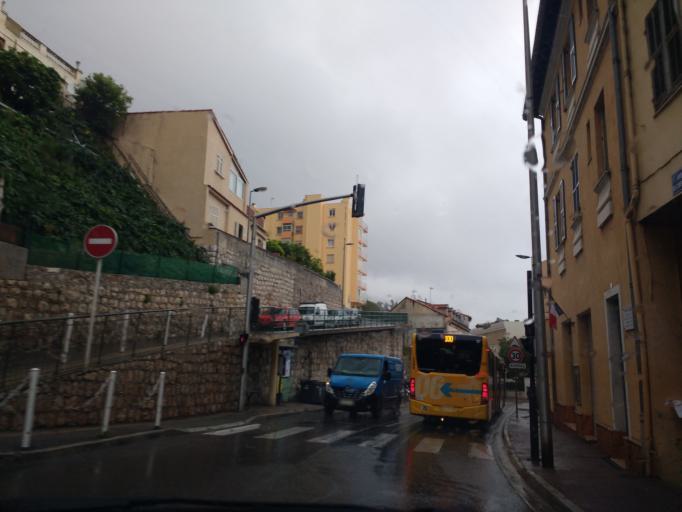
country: FR
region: Provence-Alpes-Cote d'Azur
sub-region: Departement des Alpes-Maritimes
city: Cap-d'Ail
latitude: 43.7246
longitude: 7.4088
